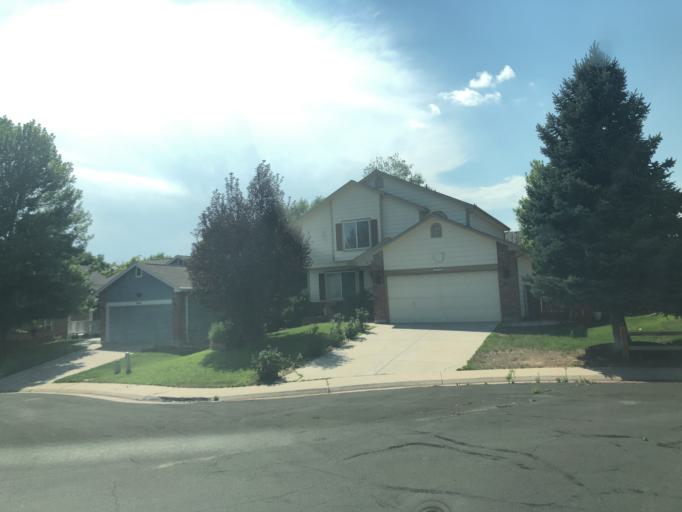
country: US
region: Colorado
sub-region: Arapahoe County
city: Dove Valley
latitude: 39.6321
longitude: -104.7571
